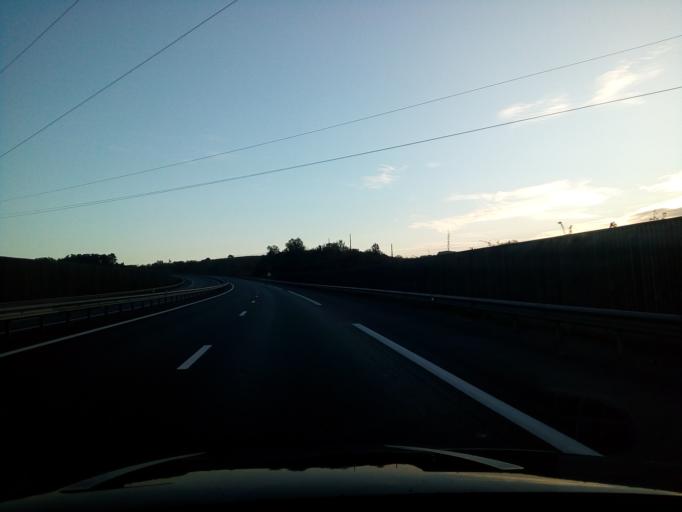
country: FR
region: Poitou-Charentes
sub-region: Departement de la Charente
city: Chateauneuf-sur-Charente
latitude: 45.5229
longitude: -0.0727
